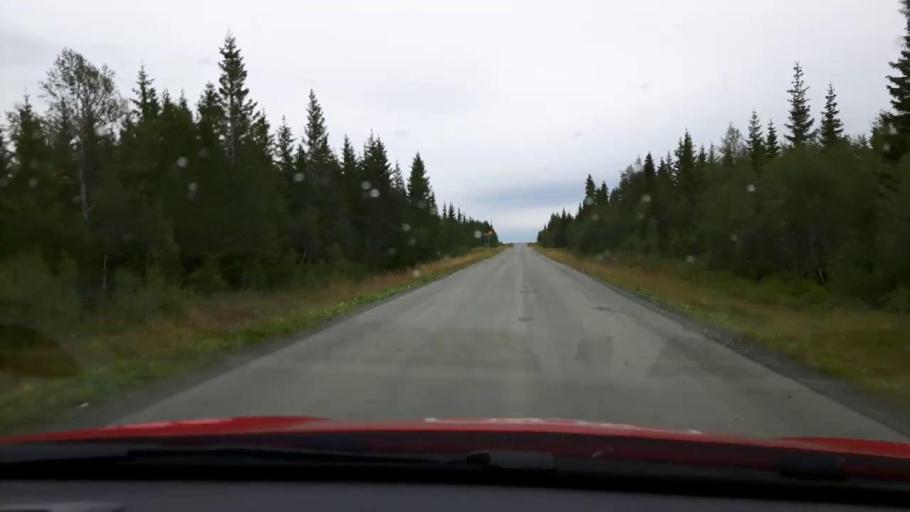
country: SE
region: Jaemtland
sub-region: Are Kommun
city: Are
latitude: 63.4482
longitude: 13.2228
